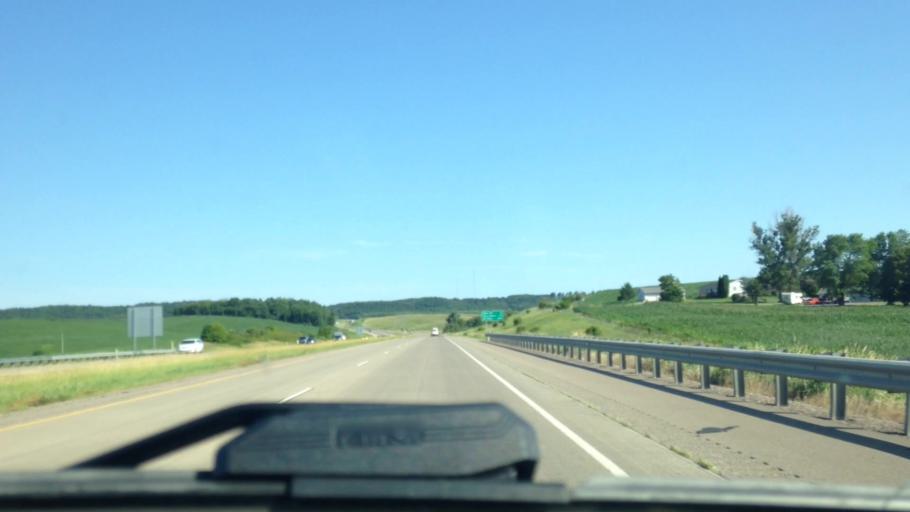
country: US
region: Wisconsin
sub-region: Trempealeau County
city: Osseo
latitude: 44.5906
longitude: -91.2132
